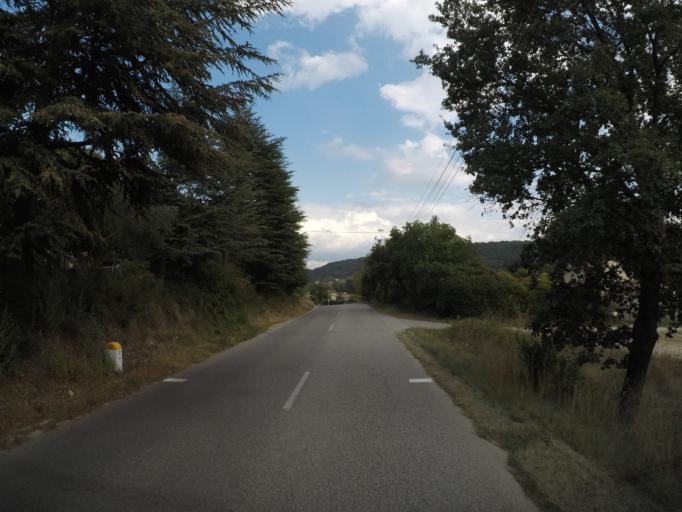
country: FR
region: Provence-Alpes-Cote d'Azur
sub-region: Departement des Alpes-de-Haute-Provence
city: Riez
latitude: 43.8163
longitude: 6.0729
